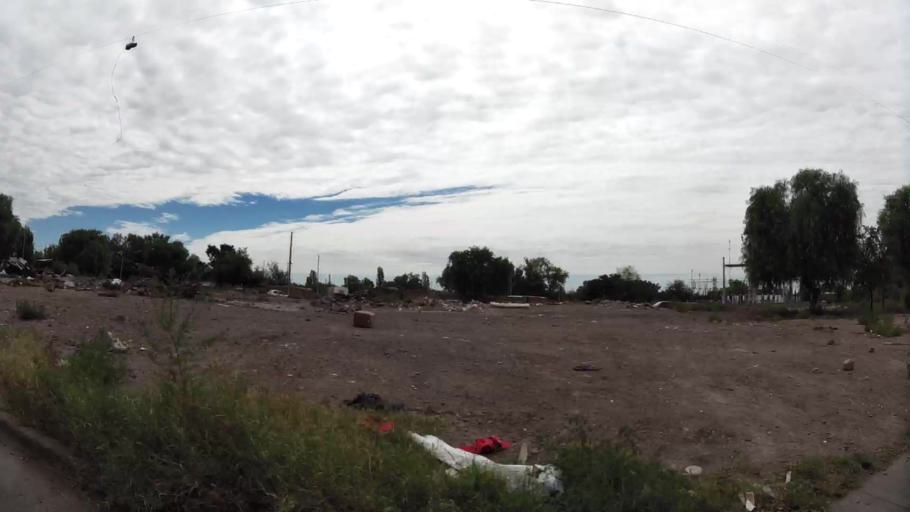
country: AR
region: Mendoza
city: Las Heras
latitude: -32.8623
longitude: -68.8608
